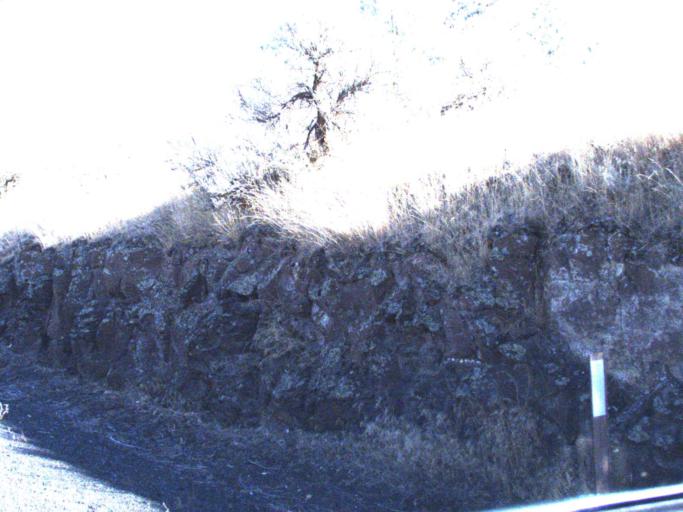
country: US
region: Washington
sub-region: Franklin County
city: Connell
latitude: 46.6461
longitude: -118.5448
